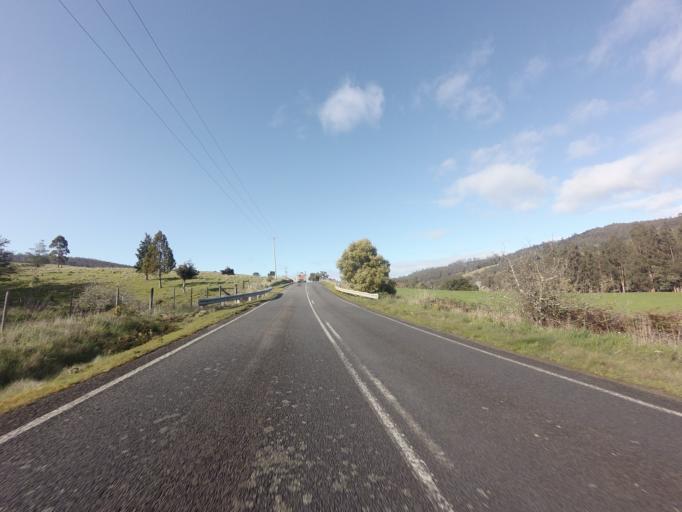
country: AU
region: Tasmania
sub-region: Huon Valley
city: Cygnet
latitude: -43.2819
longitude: 147.0107
